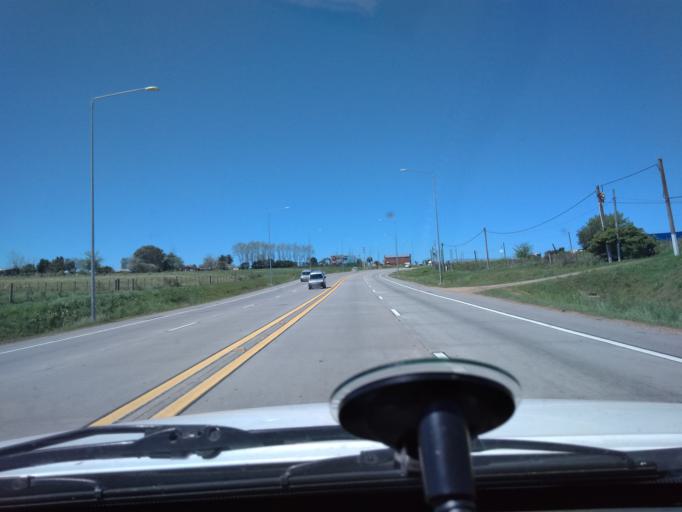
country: UY
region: Canelones
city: La Paz
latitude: -34.7933
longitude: -56.1726
